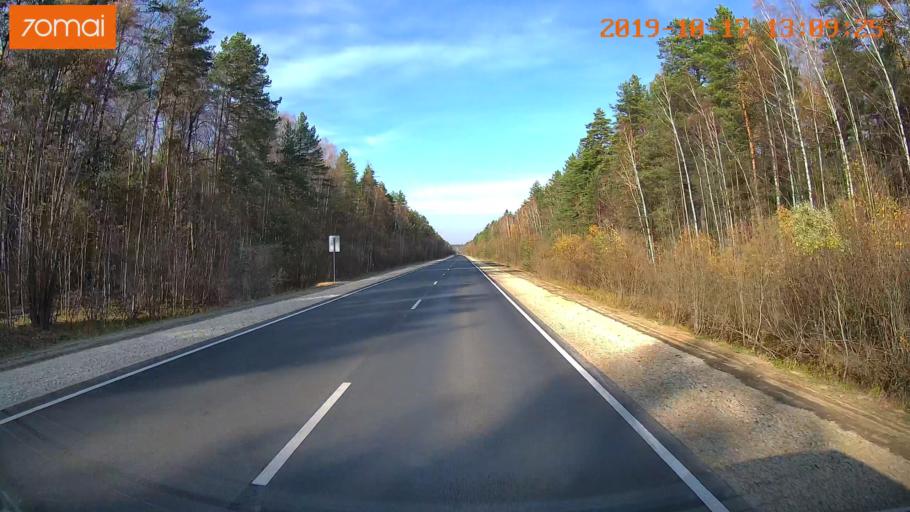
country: RU
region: Rjazan
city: Syntul
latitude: 55.0037
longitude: 41.2631
